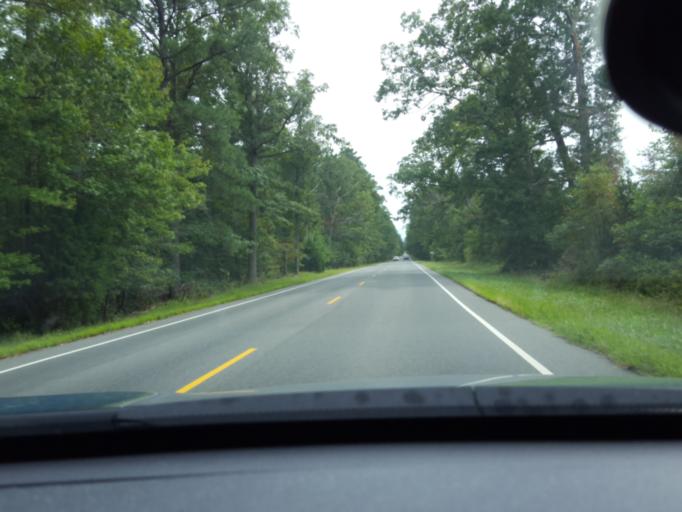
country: US
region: Virginia
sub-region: Caroline County
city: Bowling Green
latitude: 37.9810
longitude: -77.3393
